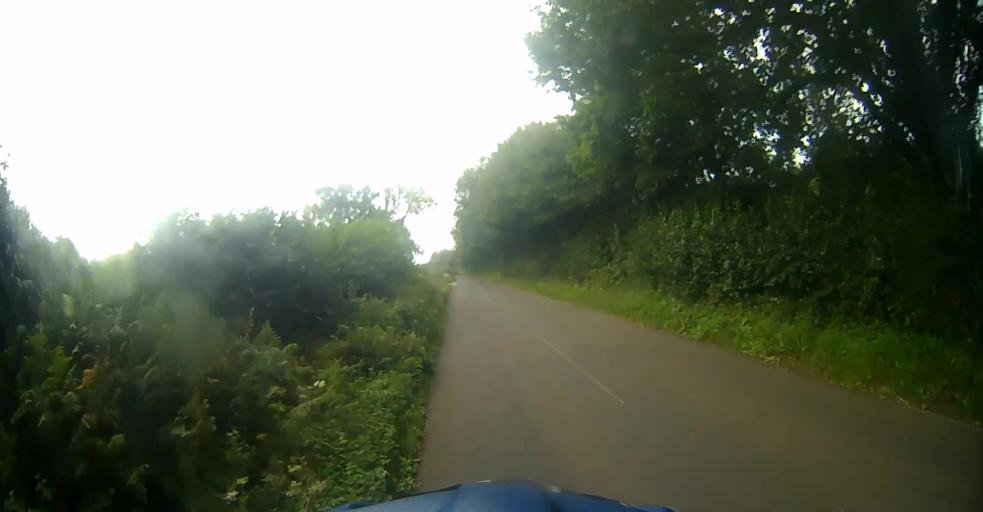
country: GB
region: England
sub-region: Hampshire
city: Alton
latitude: 51.1839
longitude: -1.0204
